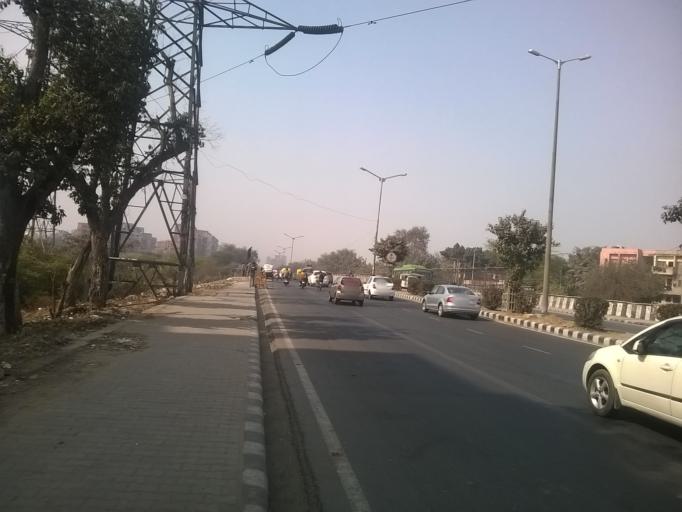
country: IN
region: NCT
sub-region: West Delhi
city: Nangloi Jat
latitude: 28.5988
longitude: 77.0626
